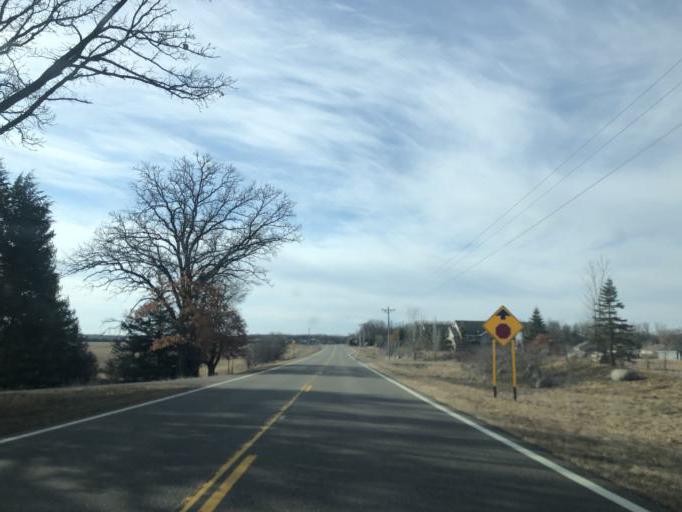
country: US
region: Minnesota
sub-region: Sherburne County
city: Becker
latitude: 45.4036
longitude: -93.8499
